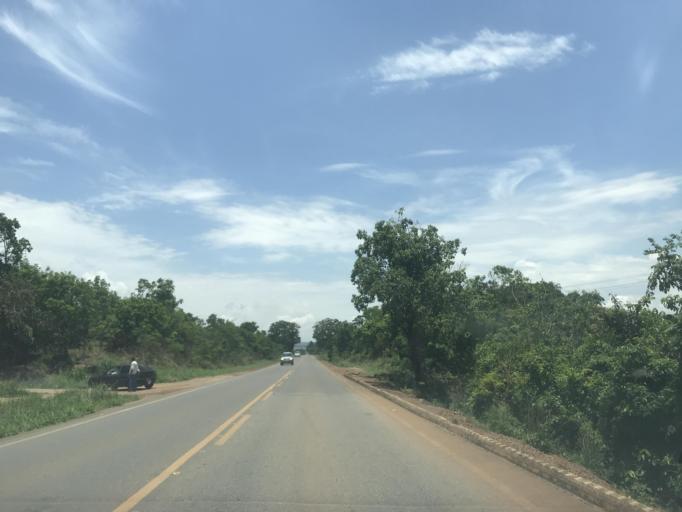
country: BR
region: Goias
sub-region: Vianopolis
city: Vianopolis
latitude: -16.6191
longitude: -48.3529
